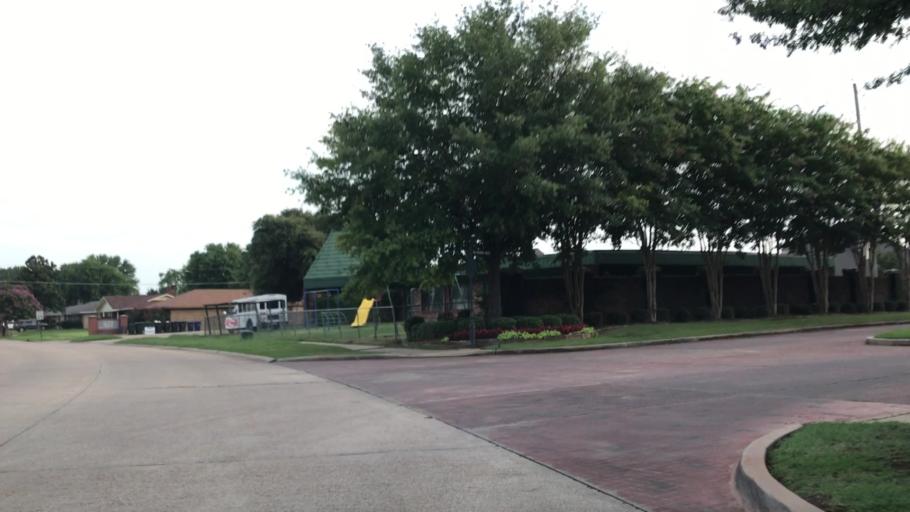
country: US
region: Louisiana
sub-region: Bossier Parish
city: Bossier City
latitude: 32.4189
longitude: -93.7073
